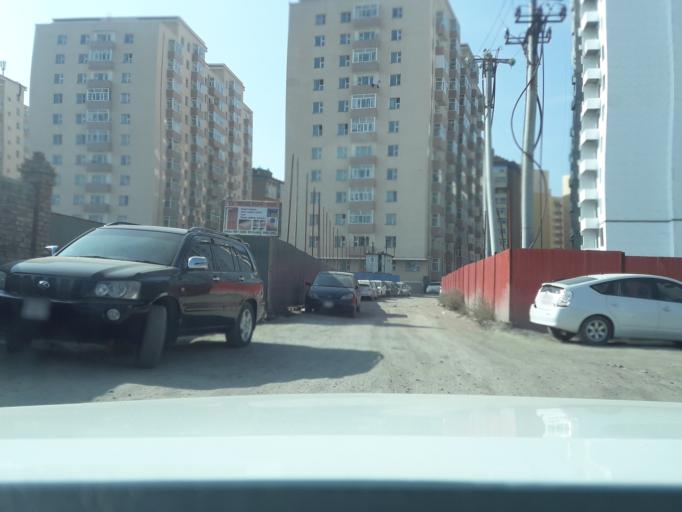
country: MN
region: Ulaanbaatar
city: Ulaanbaatar
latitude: 47.9048
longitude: 106.8835
